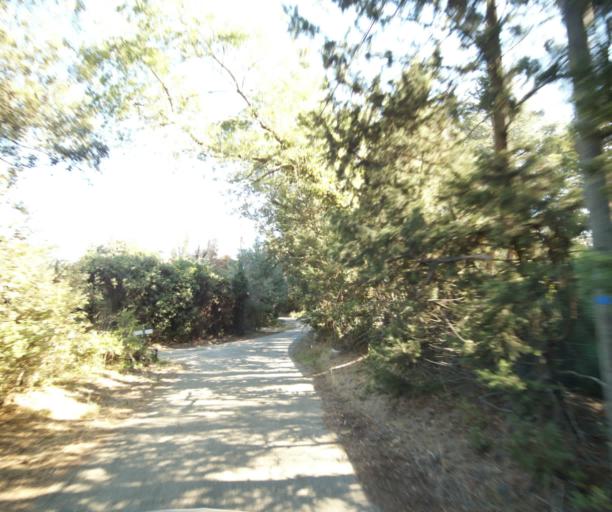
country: FR
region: Languedoc-Roussillon
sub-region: Departement du Gard
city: Bouillargues
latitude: 43.7904
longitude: 4.4171
